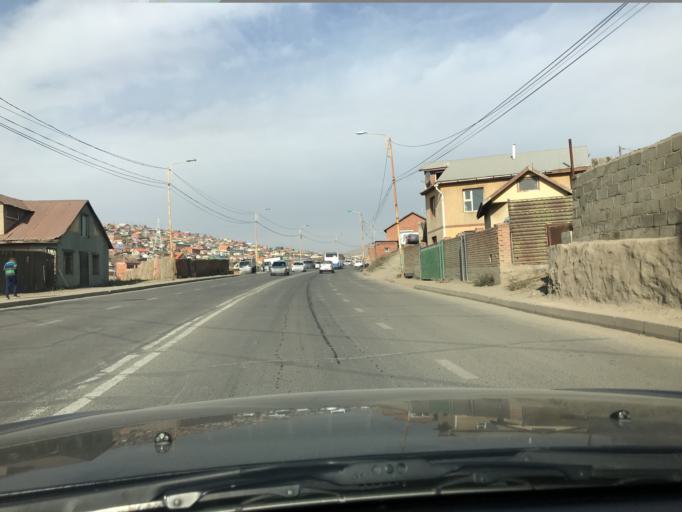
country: MN
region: Ulaanbaatar
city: Ulaanbaatar
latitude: 47.9348
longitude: 106.8853
